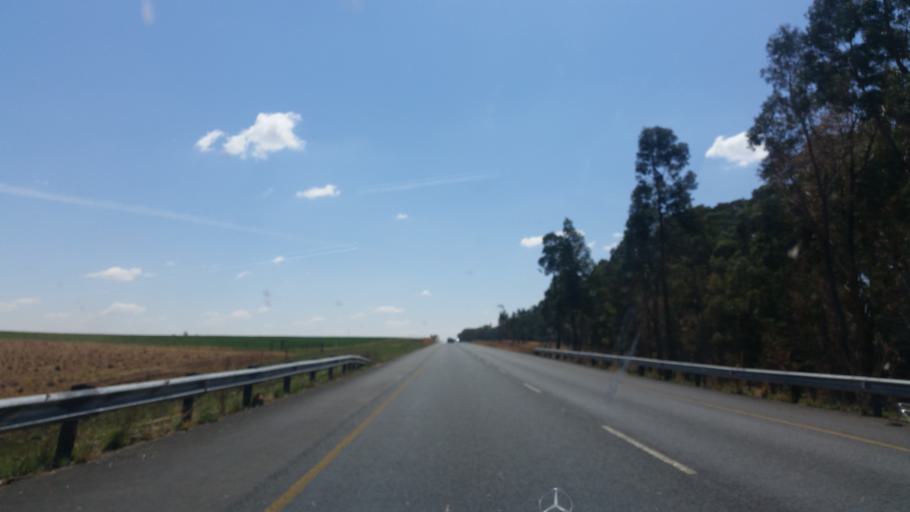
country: ZA
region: Orange Free State
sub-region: Thabo Mofutsanyana District Municipality
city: Bethlehem
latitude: -28.0991
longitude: 28.6576
